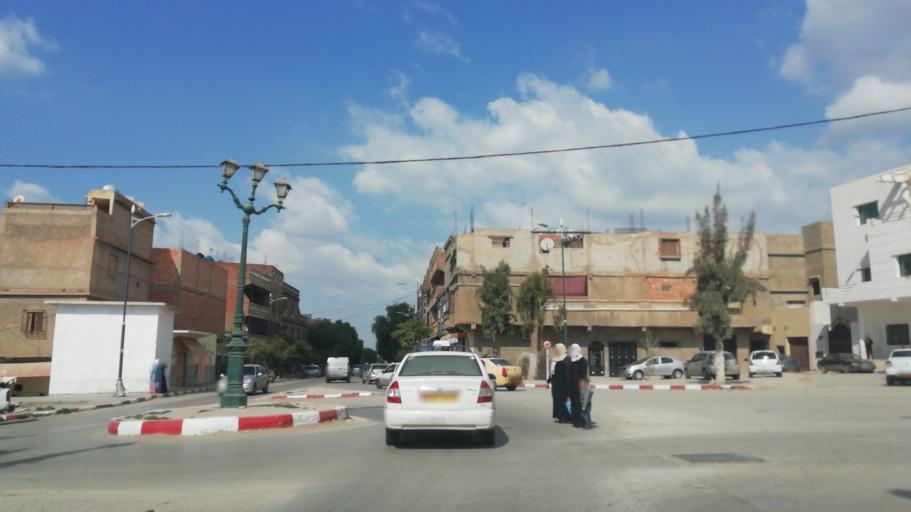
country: DZ
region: Mascara
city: Mascara
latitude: 35.5782
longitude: 0.0705
